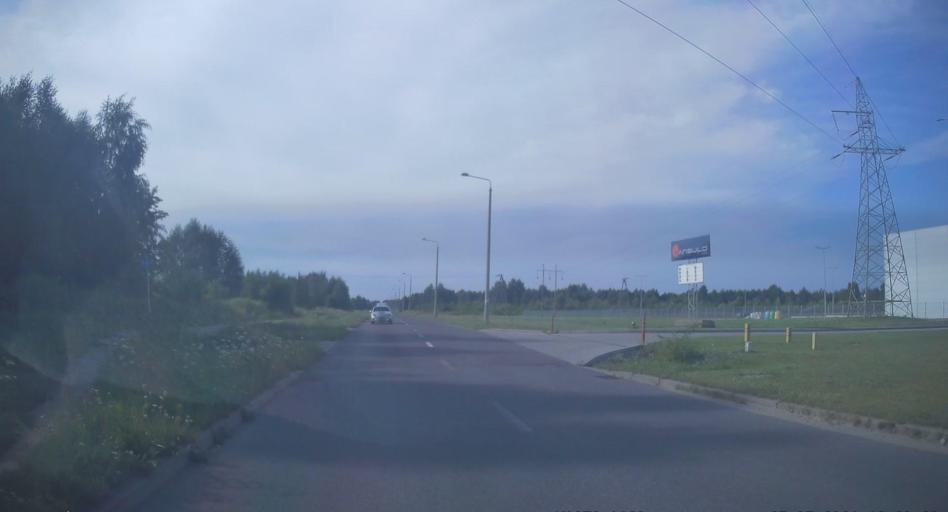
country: PL
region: Swietokrzyskie
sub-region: Powiat konecki
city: Konskie
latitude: 51.2085
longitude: 20.3968
